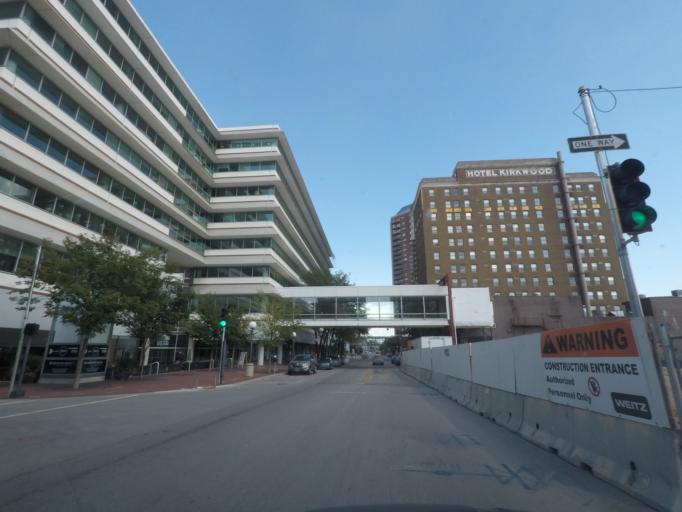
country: US
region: Iowa
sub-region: Polk County
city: Des Moines
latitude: 41.5862
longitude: -93.6234
